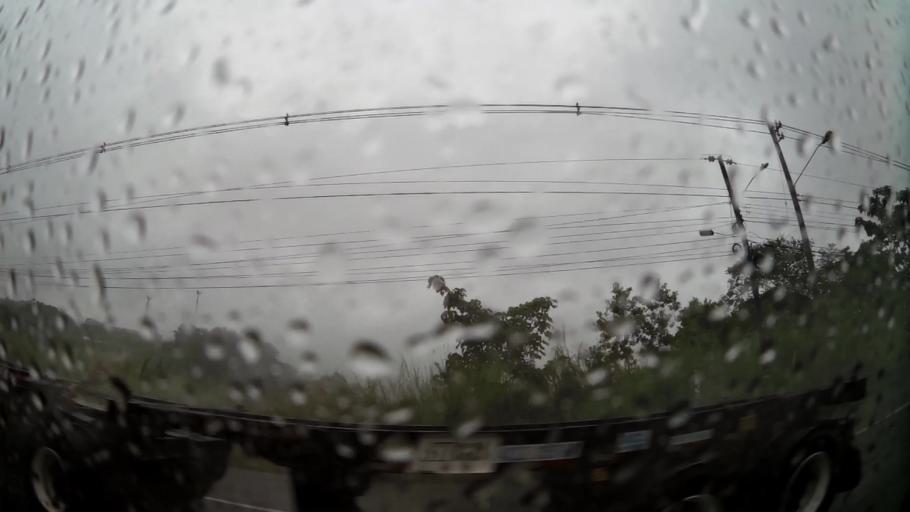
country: PA
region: Colon
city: Gatun
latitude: 9.2844
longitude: -79.7382
